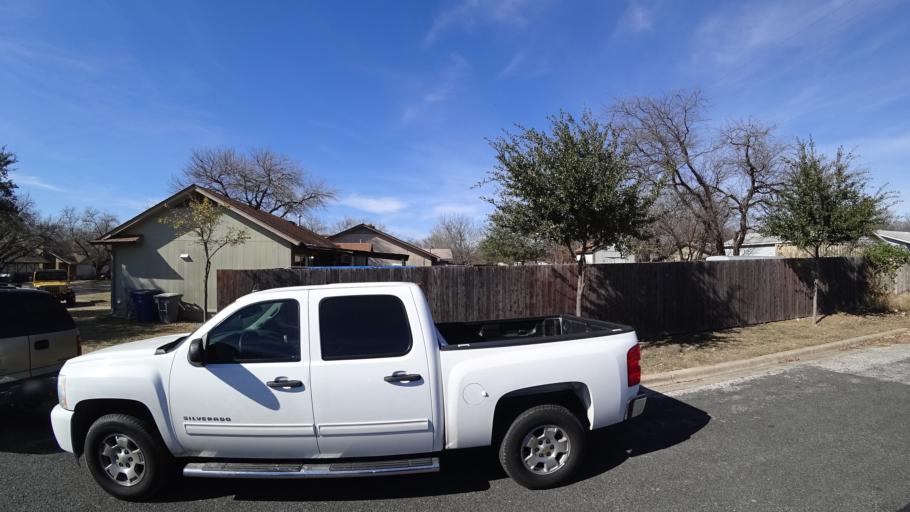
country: US
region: Texas
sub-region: Travis County
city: Wells Branch
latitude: 30.3707
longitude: -97.6867
